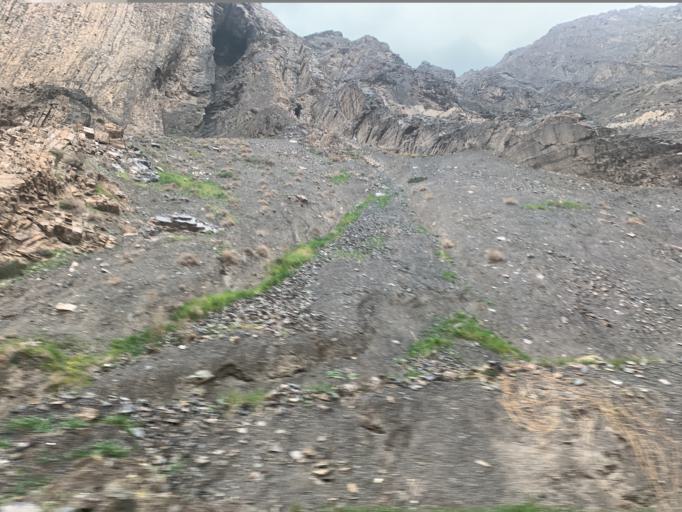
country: IR
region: Mazandaran
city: Amol
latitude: 36.1129
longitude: 52.2813
